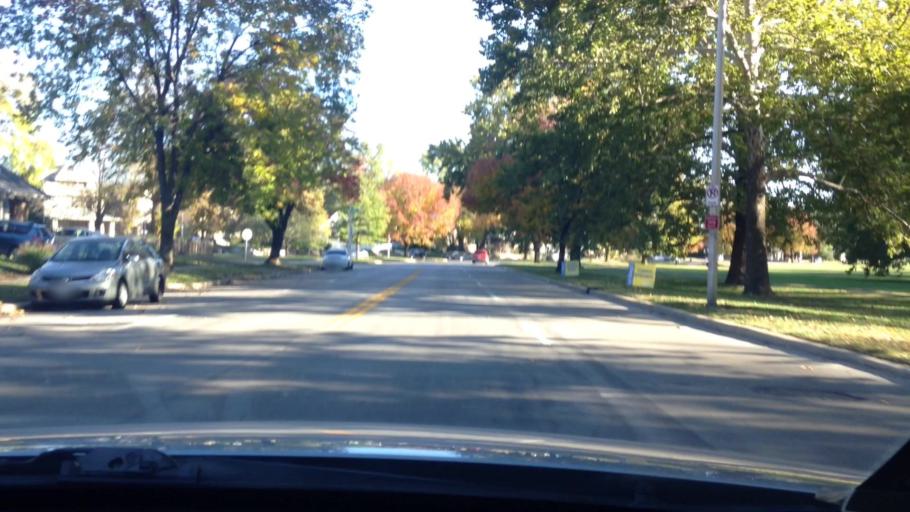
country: US
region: Kansas
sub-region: Johnson County
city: Westwood
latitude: 39.0458
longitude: -94.5752
